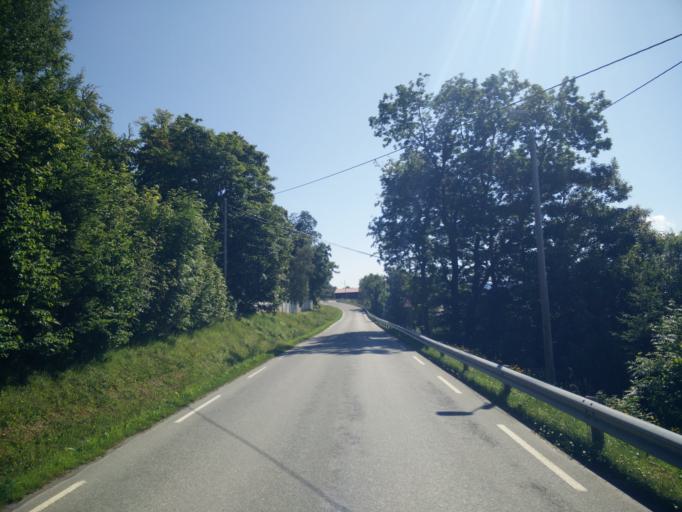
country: NO
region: More og Romsdal
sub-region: Kristiansund
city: Rensvik
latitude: 63.0269
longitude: 7.7932
